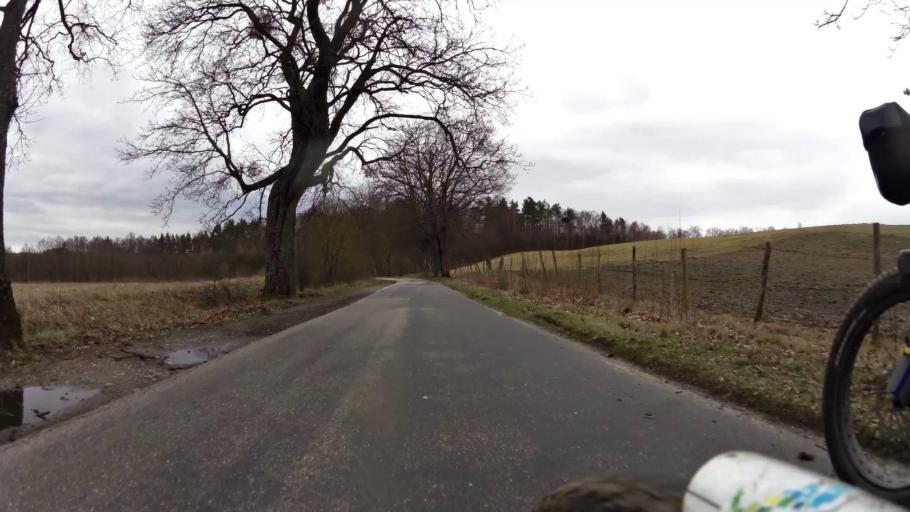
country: PL
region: Pomeranian Voivodeship
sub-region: Powiat bytowski
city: Trzebielino
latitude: 54.0993
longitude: 17.1322
